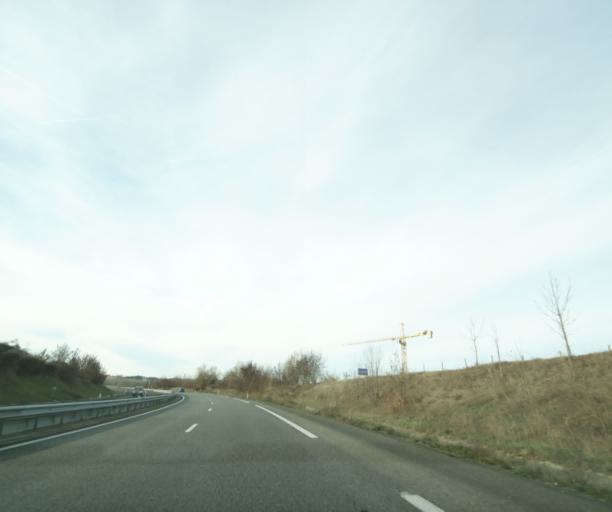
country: FR
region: Midi-Pyrenees
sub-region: Departement du Gers
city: Pujaudran
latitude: 43.6051
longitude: 1.0779
